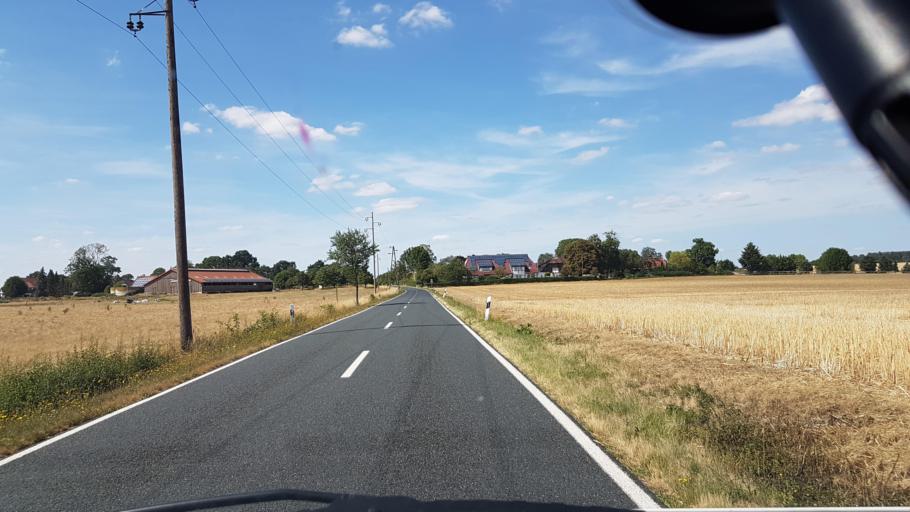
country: DE
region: Lower Saxony
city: Wolsdorf
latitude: 52.1737
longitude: 10.9506
